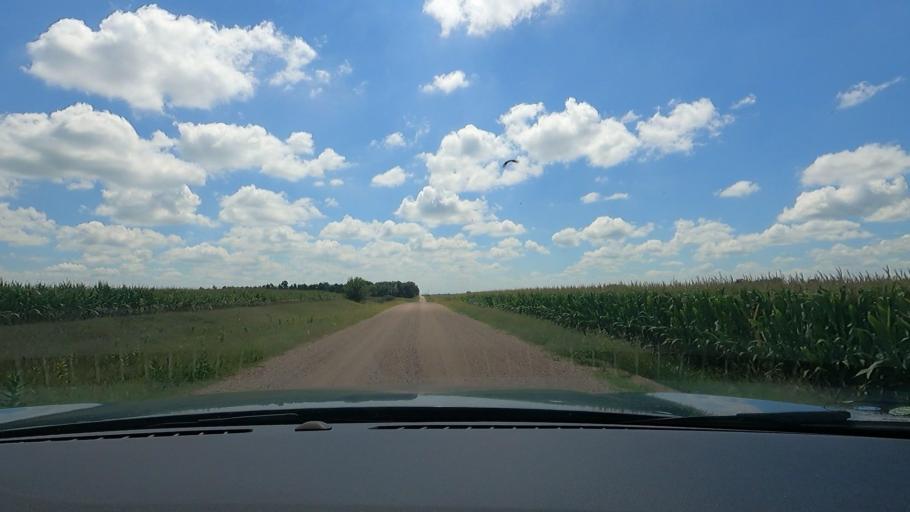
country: US
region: Nebraska
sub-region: Saunders County
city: Wahoo
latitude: 41.2697
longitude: -96.5418
